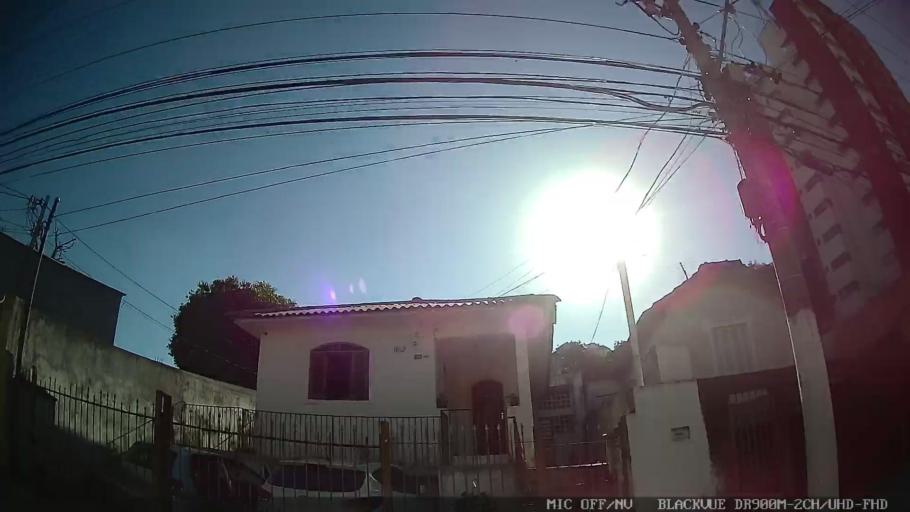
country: BR
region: Sao Paulo
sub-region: Guarulhos
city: Guarulhos
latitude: -23.5359
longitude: -46.5202
